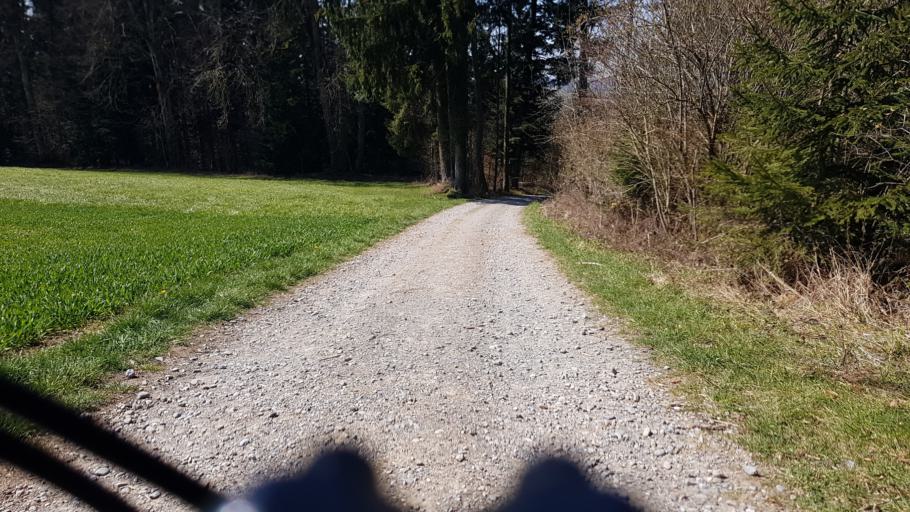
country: CH
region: Aargau
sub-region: Bezirk Kulm
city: Reinach
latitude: 47.2773
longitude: 8.1820
